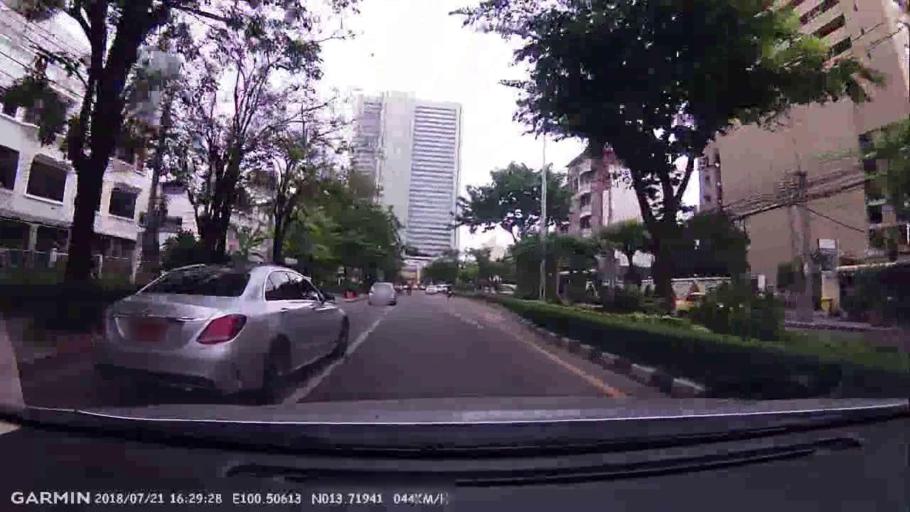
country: TH
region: Bangkok
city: Khlong San
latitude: 13.7194
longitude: 100.5062
